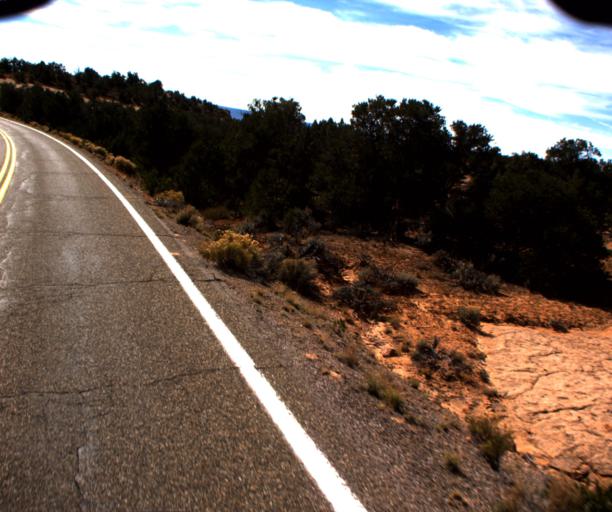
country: US
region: Arizona
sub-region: Navajo County
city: Kayenta
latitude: 36.6598
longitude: -110.5272
